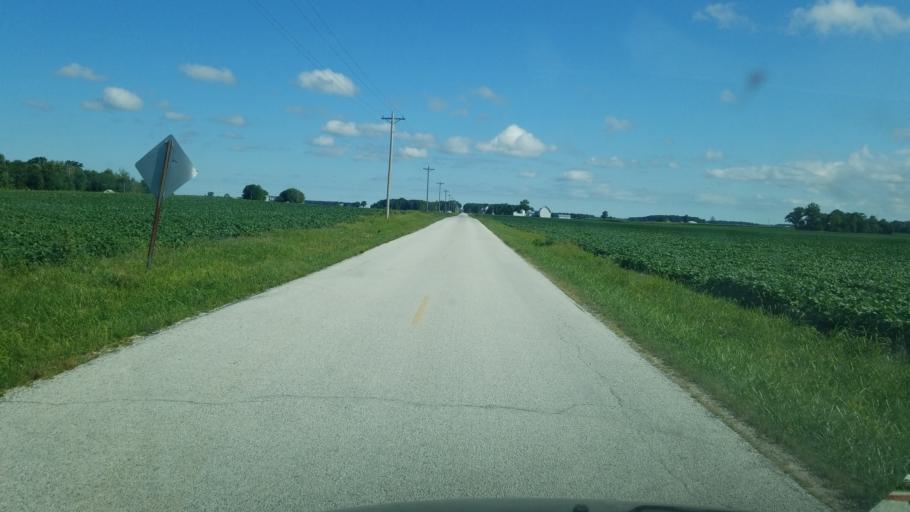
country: US
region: Ohio
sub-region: Wyandot County
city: Carey
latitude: 41.0309
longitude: -83.3630
